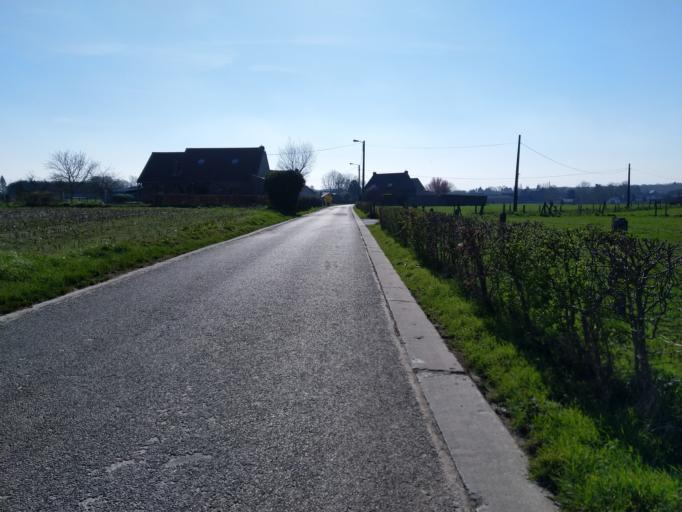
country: BE
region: Wallonia
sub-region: Province du Hainaut
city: Mons
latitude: 50.5193
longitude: 4.0089
